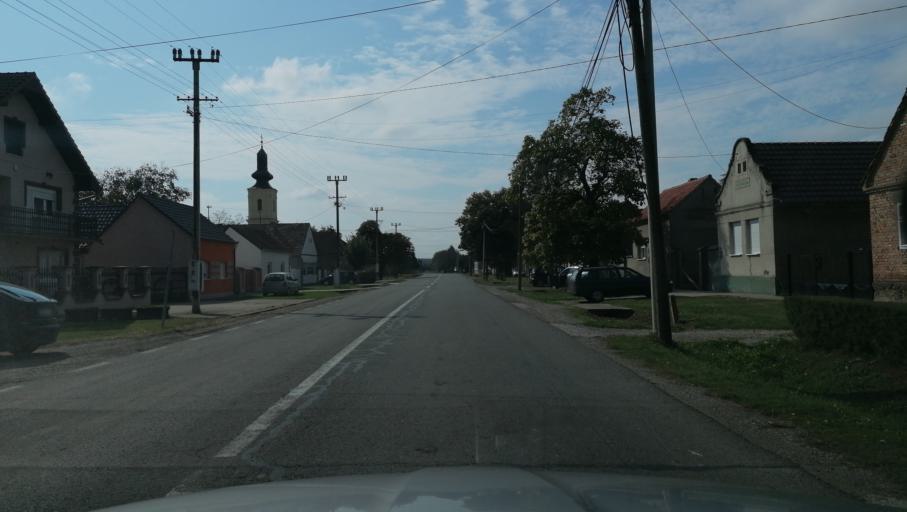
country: RS
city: Bosut
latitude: 44.9337
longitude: 19.3656
